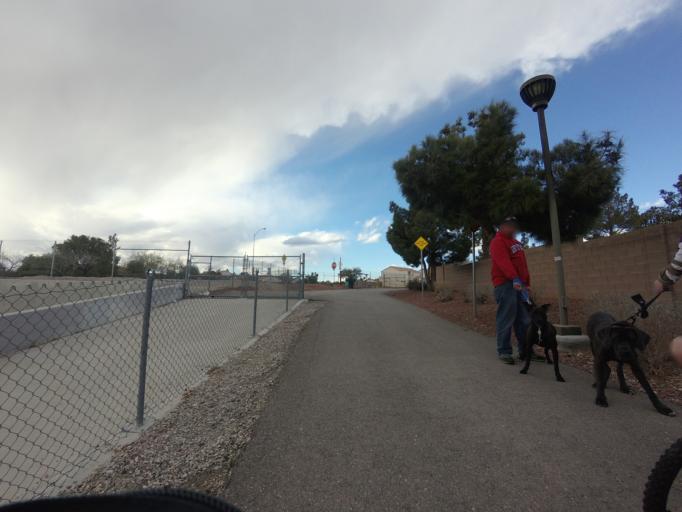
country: US
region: Nevada
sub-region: Clark County
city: North Las Vegas
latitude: 36.2648
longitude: -115.1931
